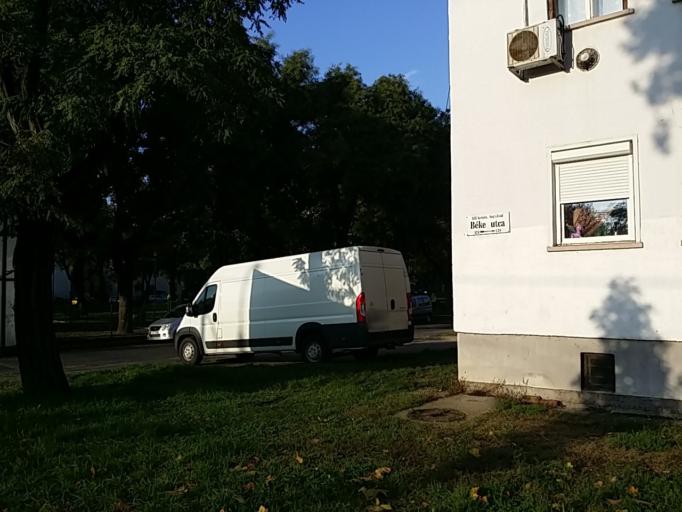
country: HU
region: Budapest
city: Budapest XIII. keruelet
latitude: 47.5446
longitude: 19.0879
